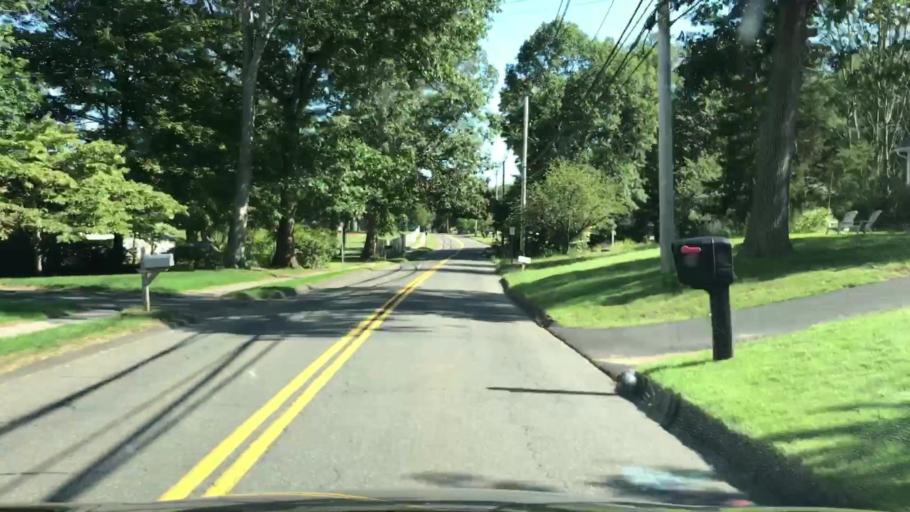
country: US
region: Connecticut
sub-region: New Haven County
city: Wallingford Center
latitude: 41.4274
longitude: -72.8290
